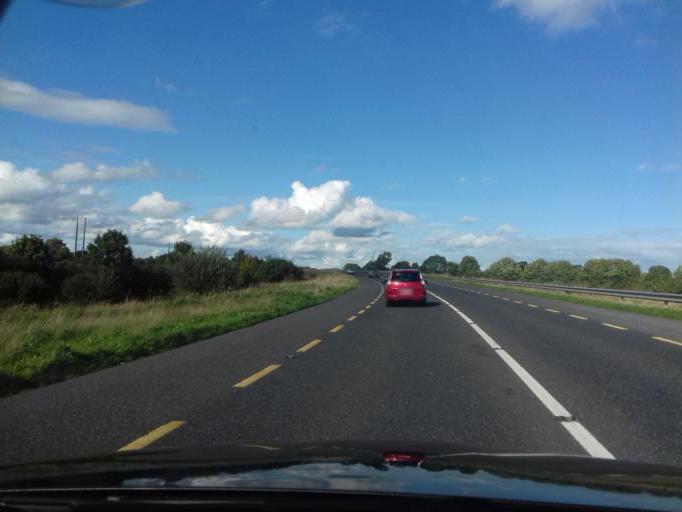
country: IE
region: Leinster
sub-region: Uibh Fhaili
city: Tullamore
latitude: 53.2586
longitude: -7.4676
